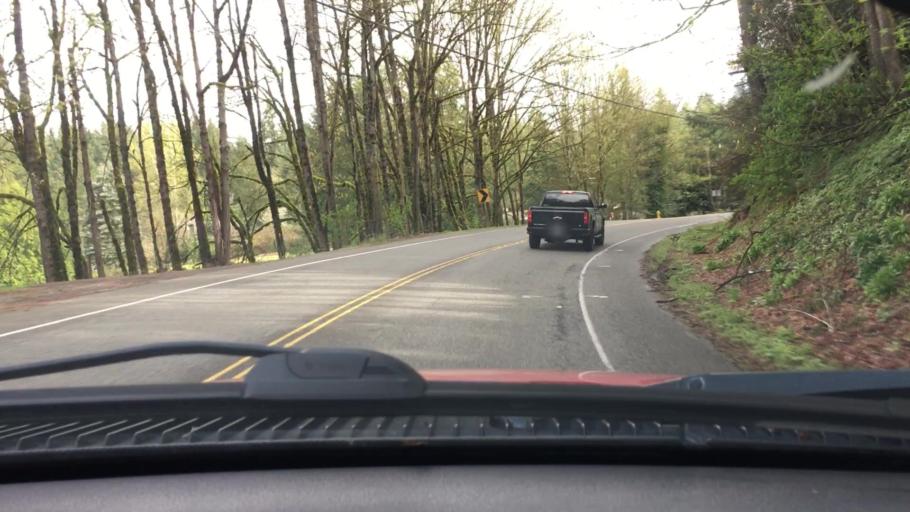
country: US
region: Washington
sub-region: King County
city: Maple Valley
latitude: 47.3754
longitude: -122.0493
